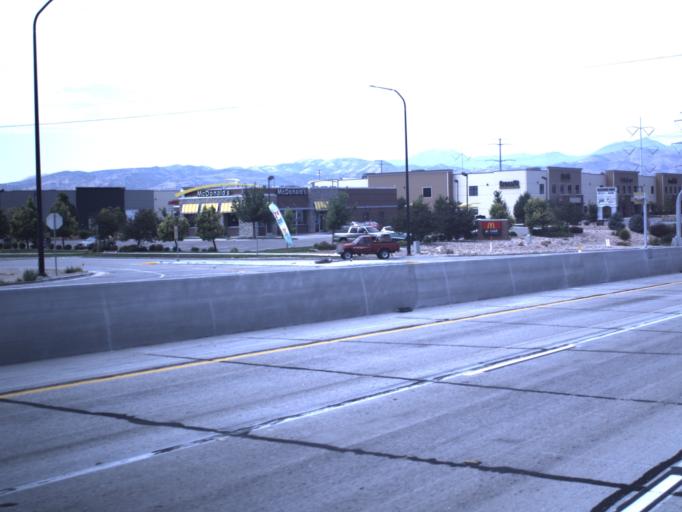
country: US
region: Utah
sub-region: Salt Lake County
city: Draper
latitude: 40.5045
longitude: -111.8965
